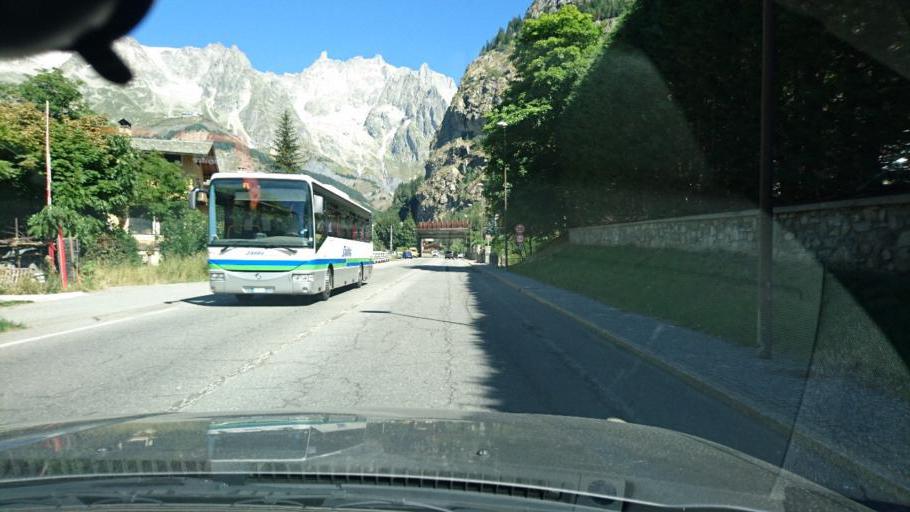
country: IT
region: Aosta Valley
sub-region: Valle d'Aosta
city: Courmayeur
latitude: 45.7982
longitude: 6.9681
